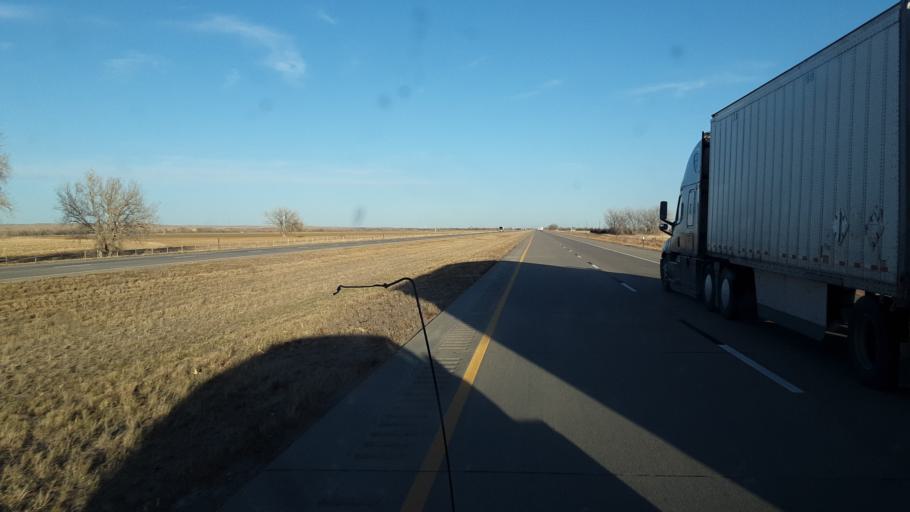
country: US
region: Nebraska
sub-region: Keith County
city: Ogallala
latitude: 41.0668
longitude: -101.9702
